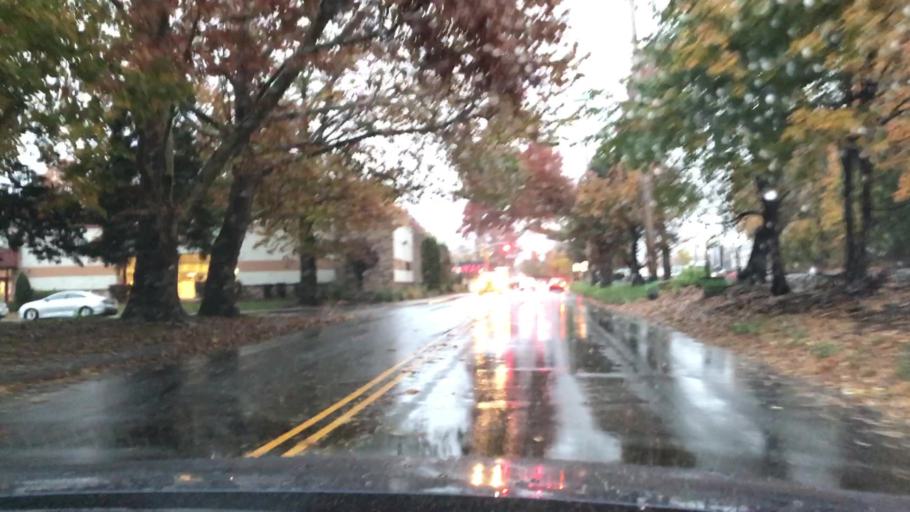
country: US
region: New Jersey
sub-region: Bergen County
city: Bergenfield
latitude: 40.9226
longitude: -73.9993
